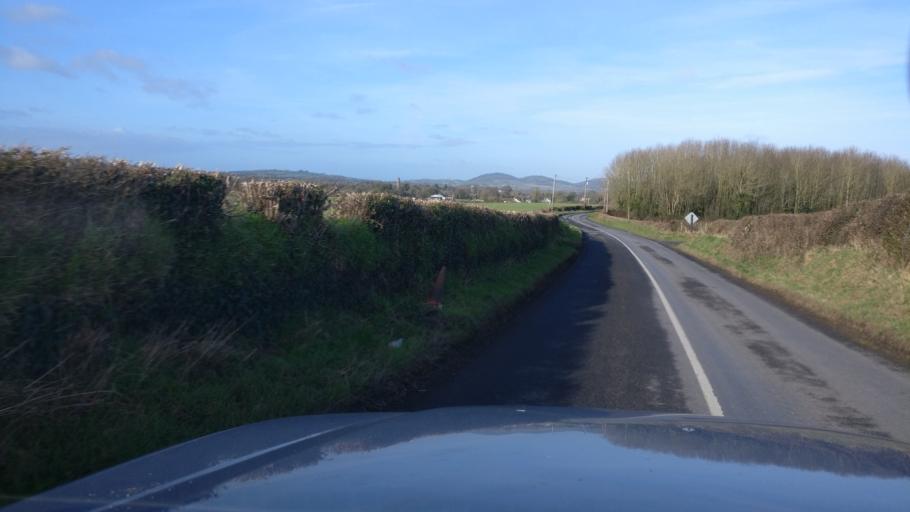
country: IE
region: Leinster
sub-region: Laois
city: Stradbally
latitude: 52.9522
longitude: -7.1986
